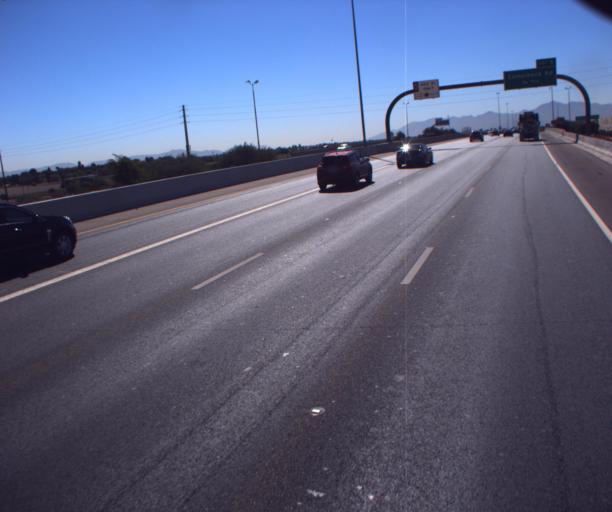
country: US
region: Arizona
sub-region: Maricopa County
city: Peoria
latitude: 33.5246
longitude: -112.2692
